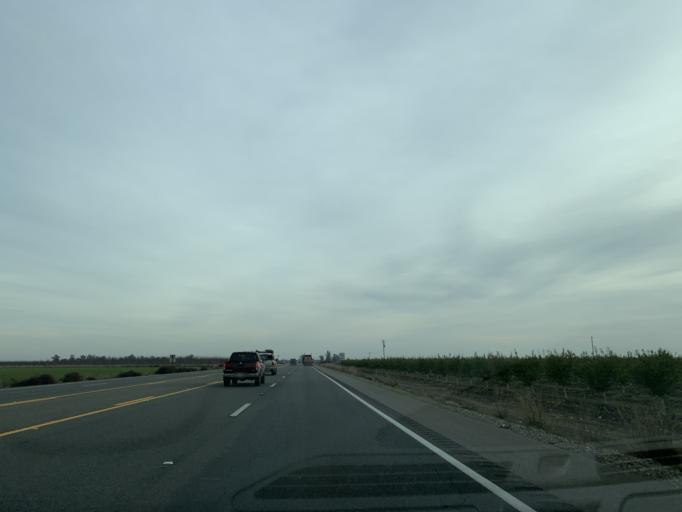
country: US
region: California
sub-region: Yuba County
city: Plumas Lake
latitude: 38.8757
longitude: -121.5625
